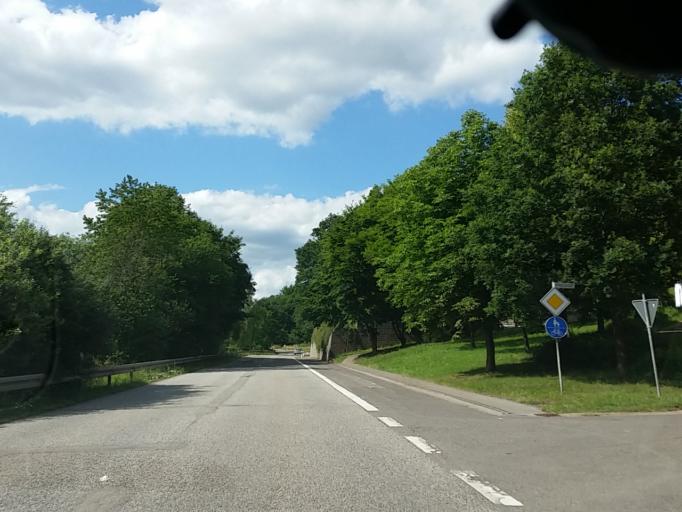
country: DE
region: Saarland
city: Wadern
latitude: 49.5136
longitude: 6.8697
